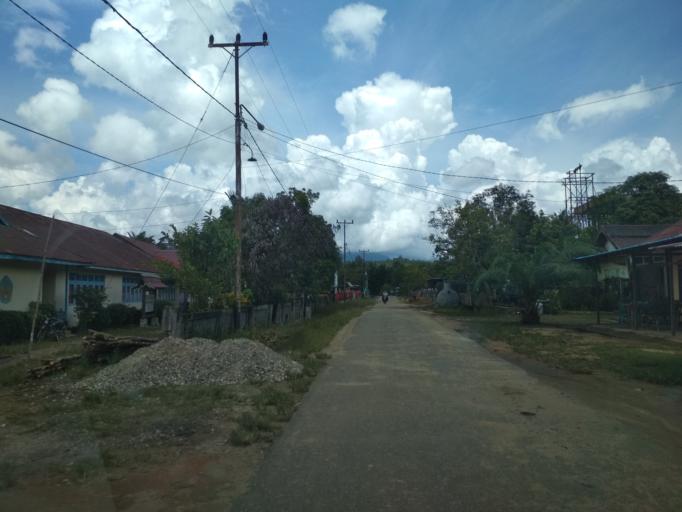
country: ID
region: West Kalimantan
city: Bengkayang
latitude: 0.7481
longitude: 110.1052
